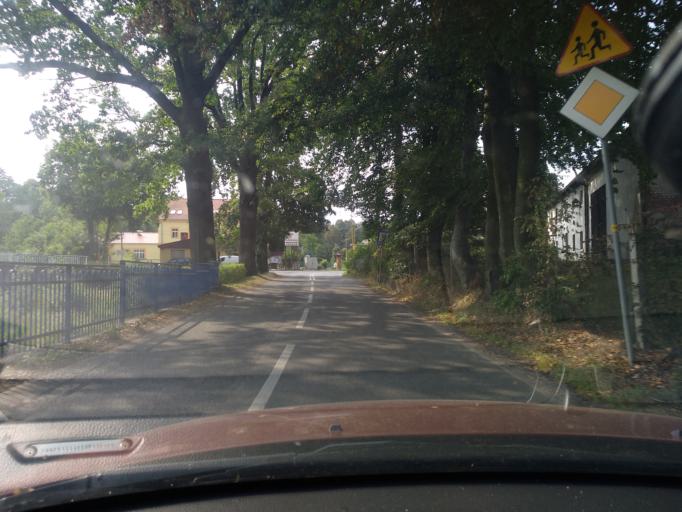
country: PL
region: Lower Silesian Voivodeship
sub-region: Powiat jeleniogorski
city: Stara Kamienica
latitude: 50.9164
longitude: 15.5728
